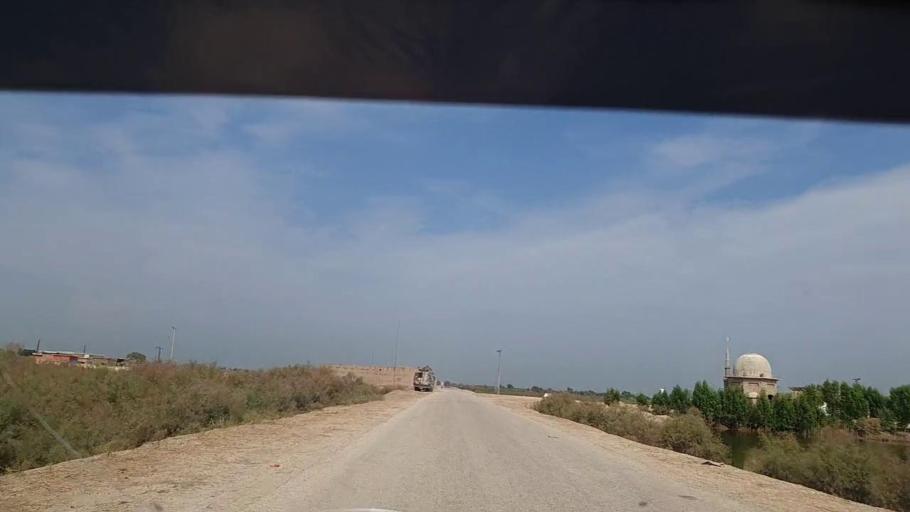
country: PK
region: Sindh
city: Thul
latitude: 28.1991
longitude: 68.7888
